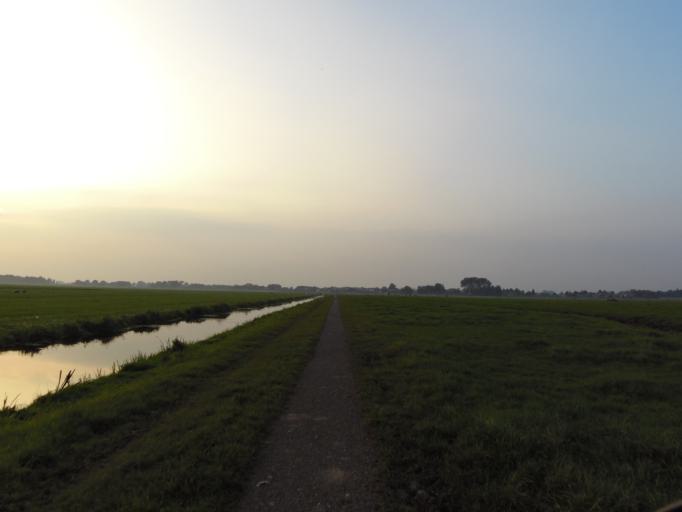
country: NL
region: South Holland
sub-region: Gemeente Rijnwoude
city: Benthuizen
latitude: 52.0980
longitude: 4.5238
